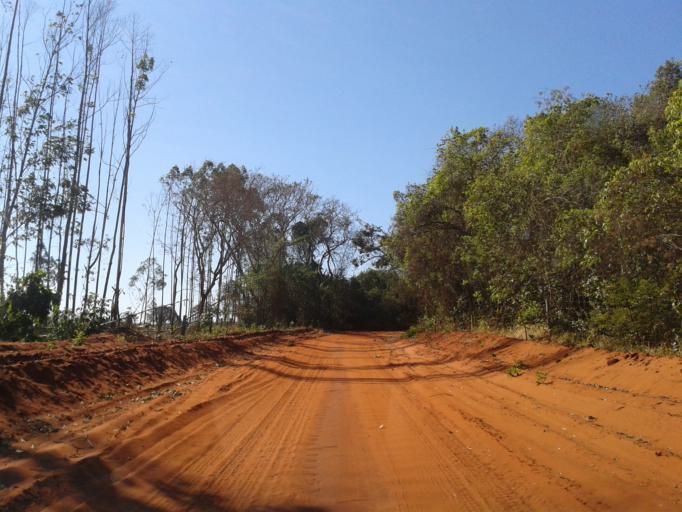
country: BR
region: Minas Gerais
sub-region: Ituiutaba
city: Ituiutaba
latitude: -19.0357
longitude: -49.3052
